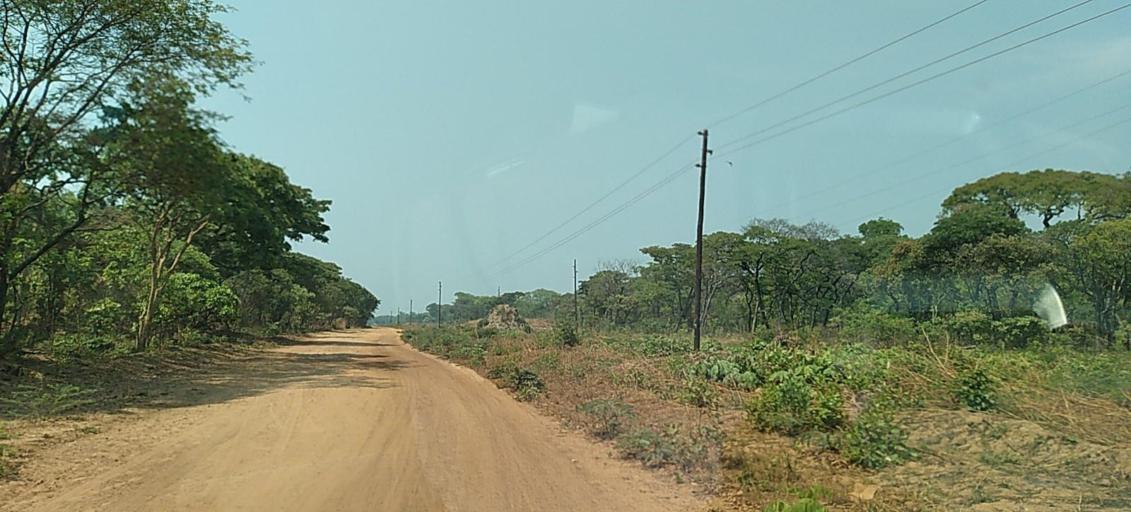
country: ZM
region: Copperbelt
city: Kalulushi
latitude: -13.0946
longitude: 27.4063
